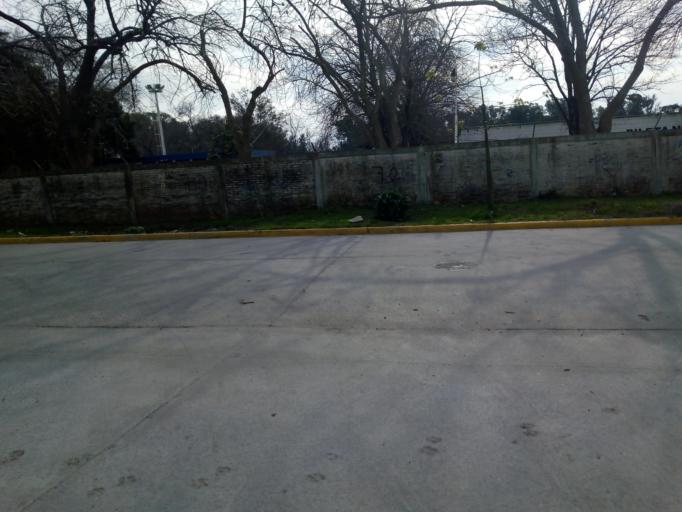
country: AR
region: Buenos Aires
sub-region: Partido de La Plata
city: La Plata
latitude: -34.8948
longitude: -57.9349
